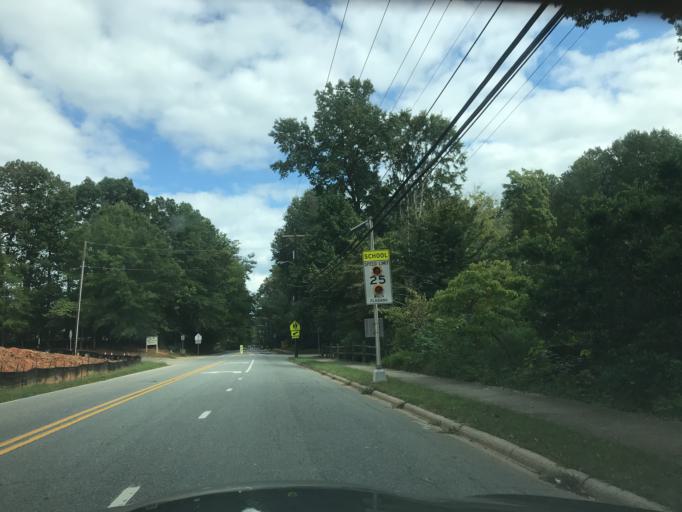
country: US
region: North Carolina
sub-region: Orange County
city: Chapel Hill
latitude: 35.9351
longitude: -79.0488
